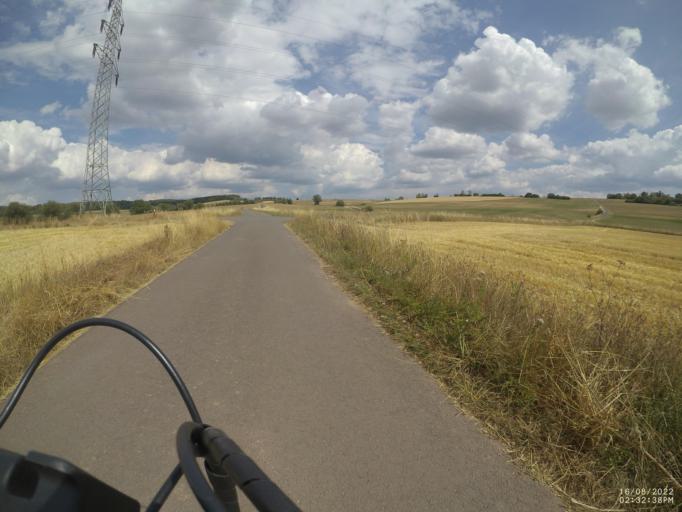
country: DE
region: Rheinland-Pfalz
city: Hillesheim
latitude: 50.3068
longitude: 6.6807
